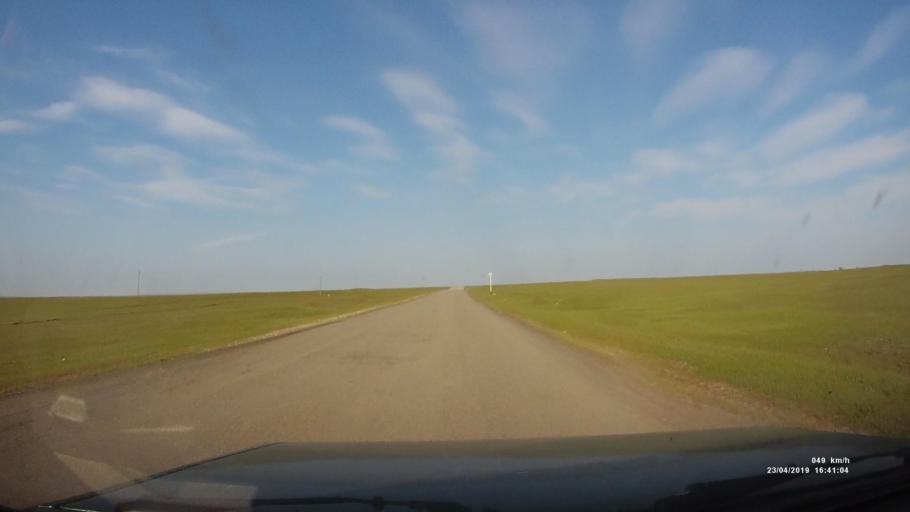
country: RU
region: Kalmykiya
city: Priyutnoye
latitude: 46.3448
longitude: 43.1830
